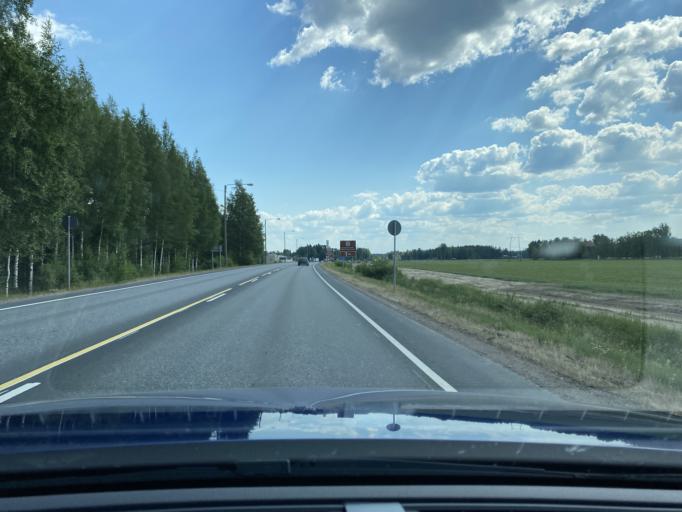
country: FI
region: Satakunta
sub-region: Rauma
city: Eura
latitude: 61.1359
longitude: 22.1208
